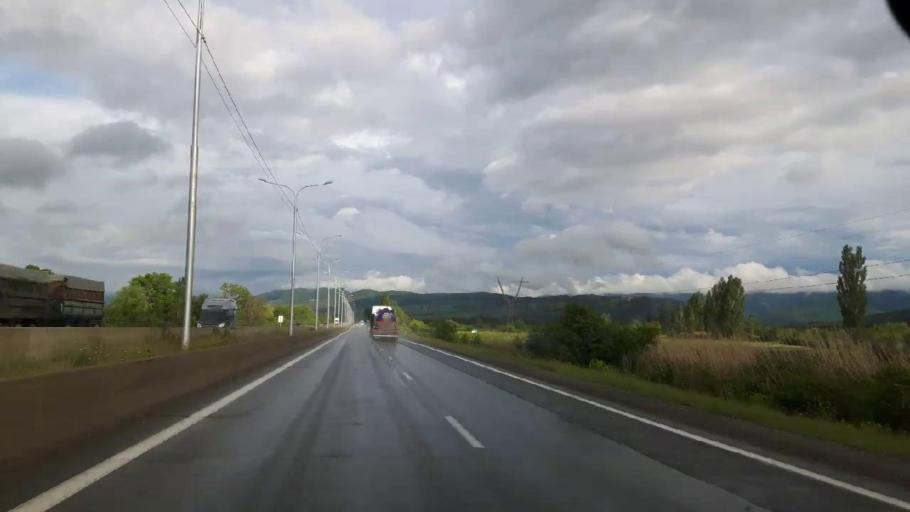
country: GE
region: Shida Kartli
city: Kaspi
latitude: 41.9228
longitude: 44.5436
